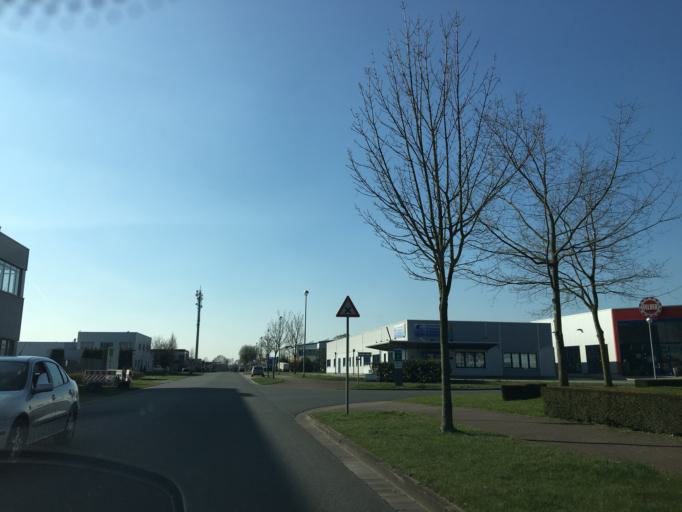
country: DE
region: North Rhine-Westphalia
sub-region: Regierungsbezirk Munster
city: Greven
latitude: 52.1092
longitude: 7.6267
